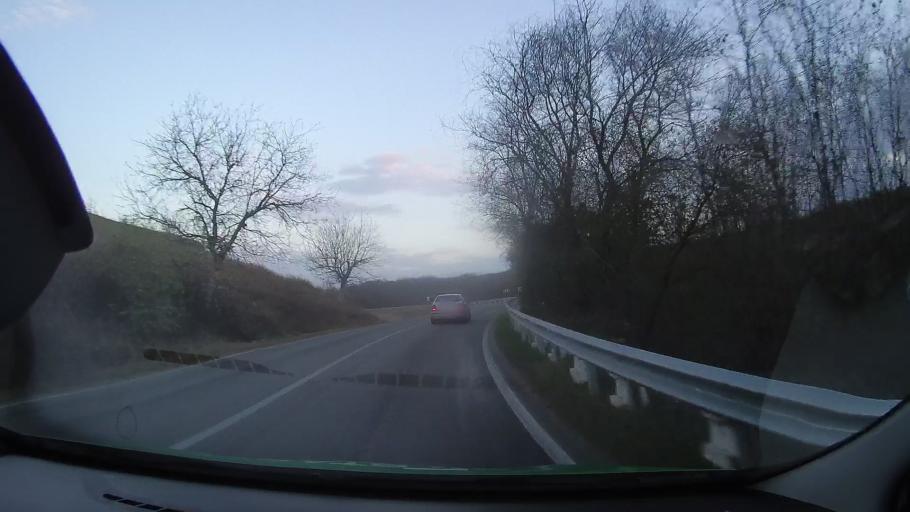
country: RO
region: Constanta
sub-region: Comuna Baneasa
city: Baneasa
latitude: 44.0766
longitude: 27.6722
